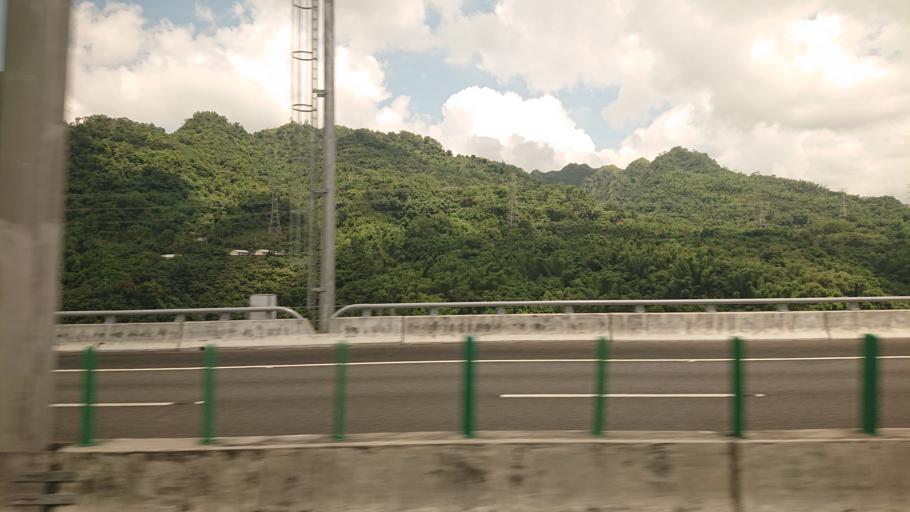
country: TW
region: Taiwan
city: Zhongxing New Village
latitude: 24.0013
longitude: 120.8069
